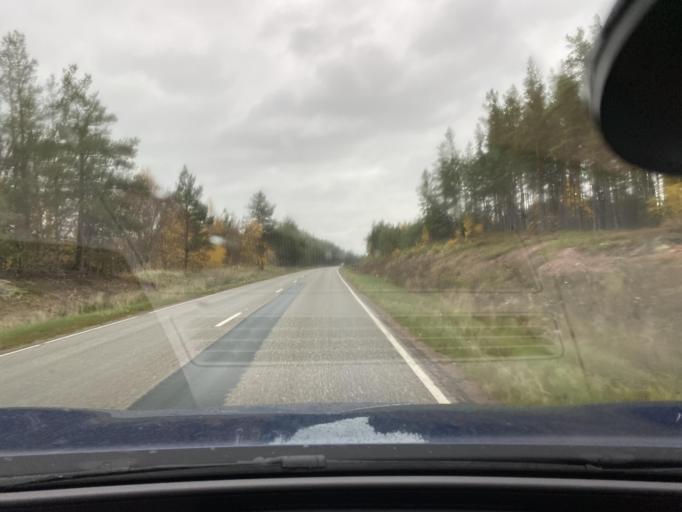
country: FI
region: Satakunta
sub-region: Rauma
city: Saekylae
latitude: 61.0555
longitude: 22.4542
